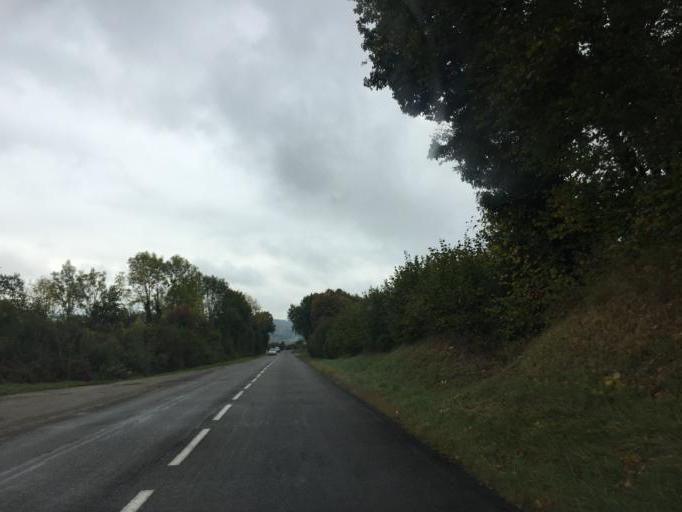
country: FR
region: Franche-Comte
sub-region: Departement du Jura
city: Orgelet
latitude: 46.4995
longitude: 5.5874
